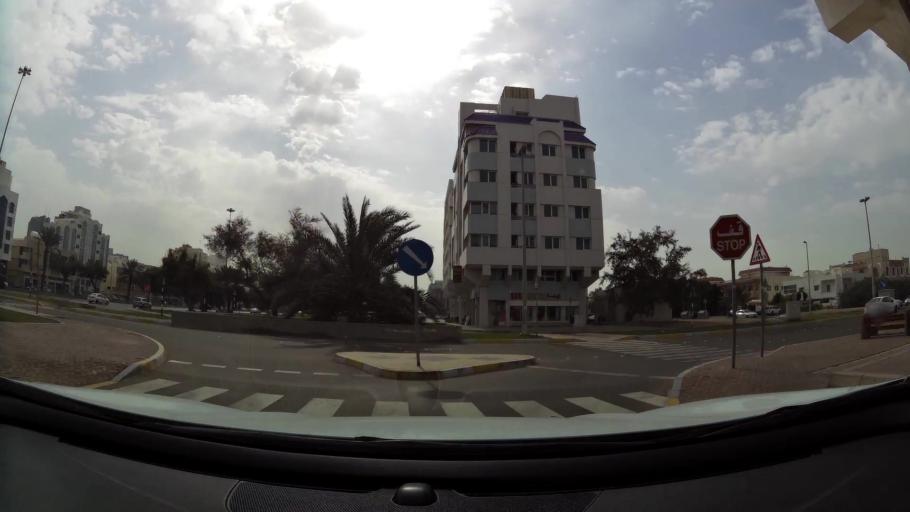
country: AE
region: Abu Dhabi
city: Abu Dhabi
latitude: 24.4547
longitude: 54.3845
